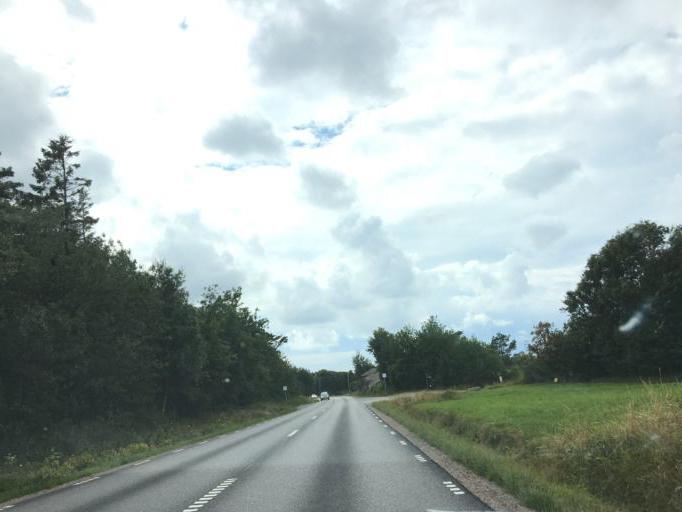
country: SE
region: Vaestra Goetaland
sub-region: Sotenas Kommun
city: Kungshamn
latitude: 58.4067
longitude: 11.2706
